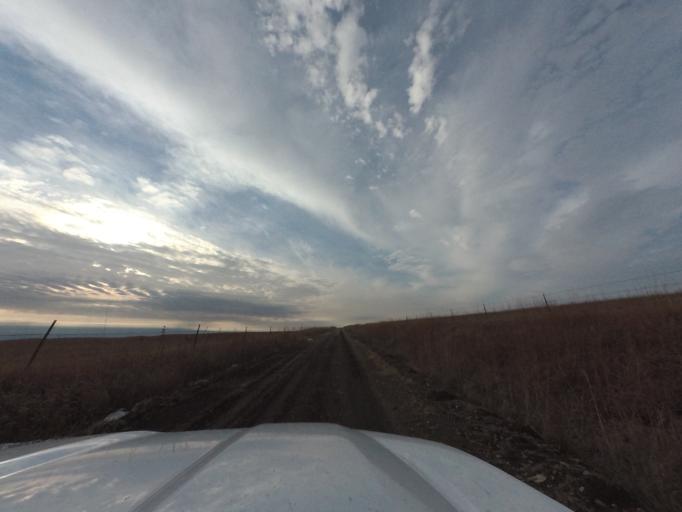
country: US
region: Kansas
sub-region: Chase County
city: Cottonwood Falls
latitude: 38.4596
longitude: -96.4471
